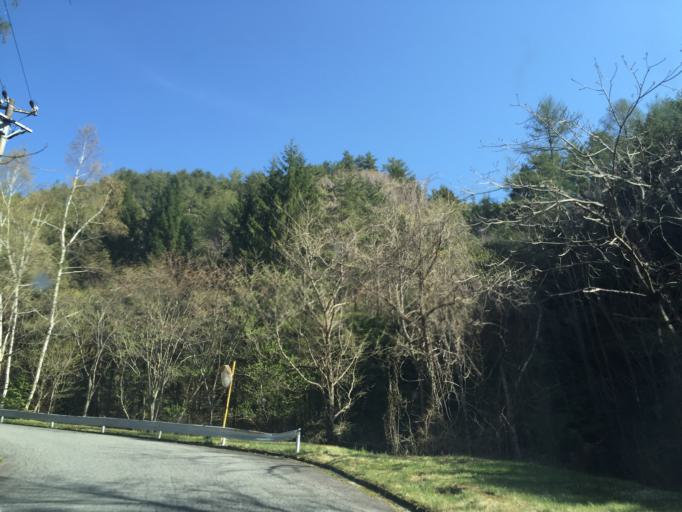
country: JP
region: Nagano
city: Iida
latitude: 35.4091
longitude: 137.6740
